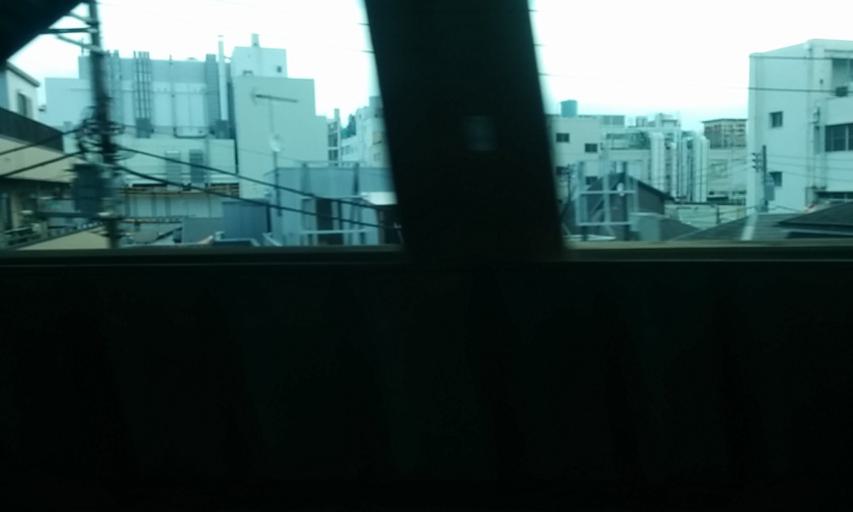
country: JP
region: Saitama
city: Kawaguchi
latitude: 35.7723
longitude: 139.7223
